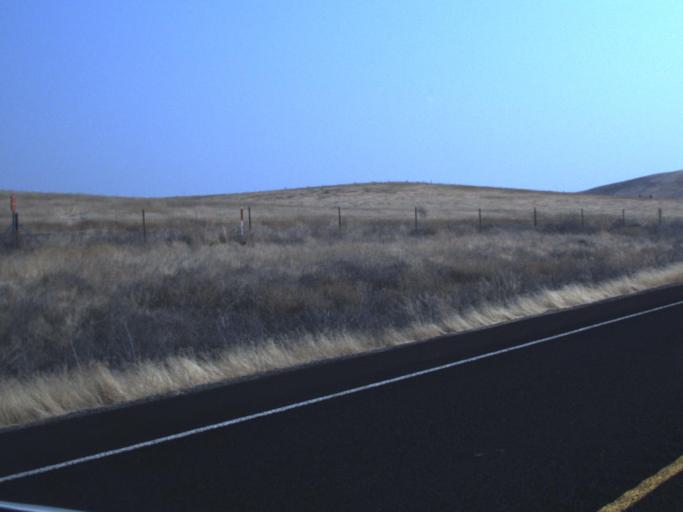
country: US
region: Washington
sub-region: Yakima County
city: Zillah
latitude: 46.5019
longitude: -120.1396
